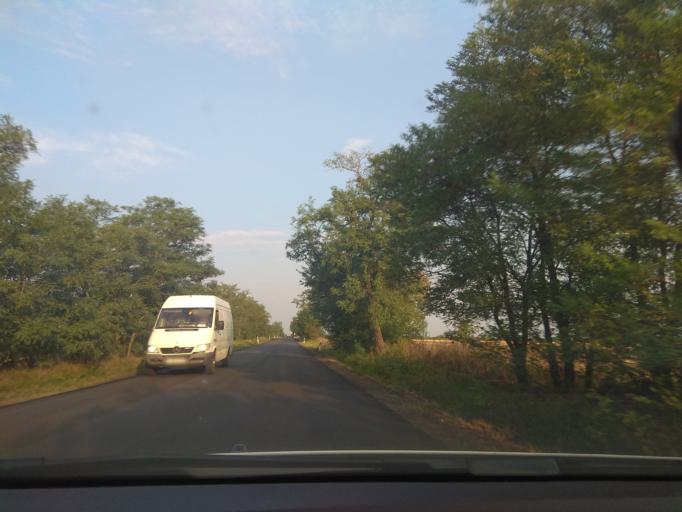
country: HU
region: Heves
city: Szihalom
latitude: 47.8174
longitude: 20.5111
